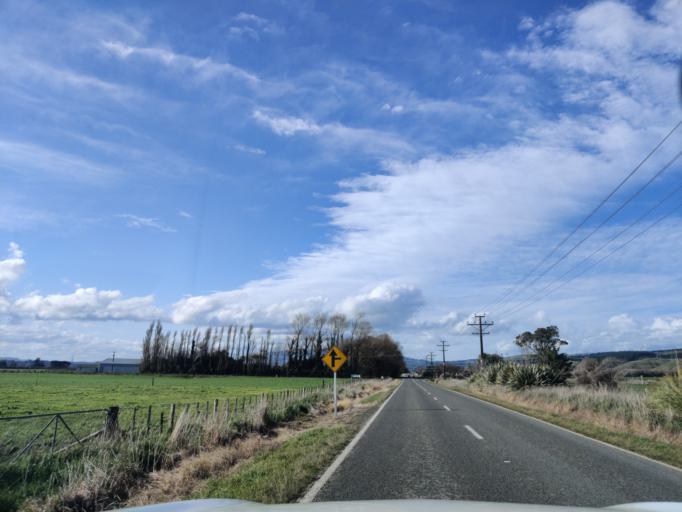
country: NZ
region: Manawatu-Wanganui
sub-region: Palmerston North City
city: Palmerston North
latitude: -40.3496
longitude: 175.7001
